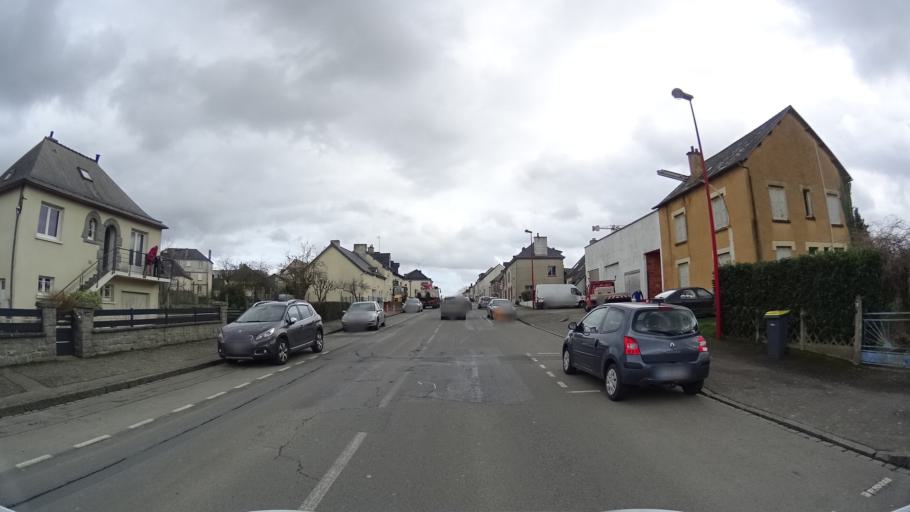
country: FR
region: Brittany
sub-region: Departement d'Ille-et-Vilaine
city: Saint-Gilles
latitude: 48.1561
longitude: -1.8313
